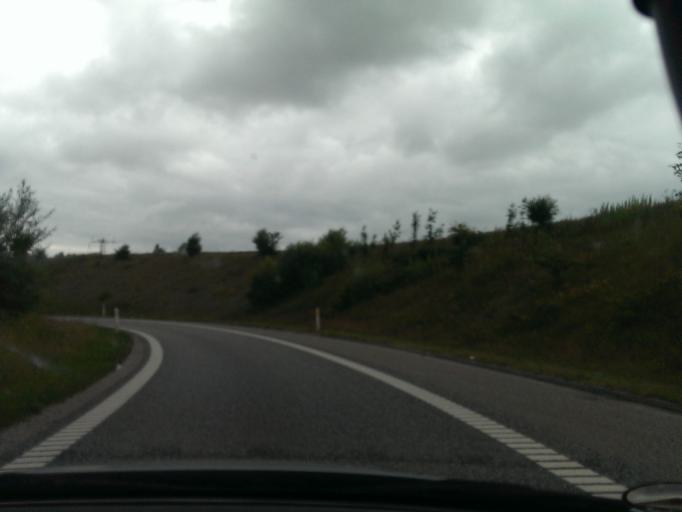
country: DK
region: Central Jutland
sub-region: Arhus Kommune
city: Sabro
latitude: 56.1907
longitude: 10.0755
